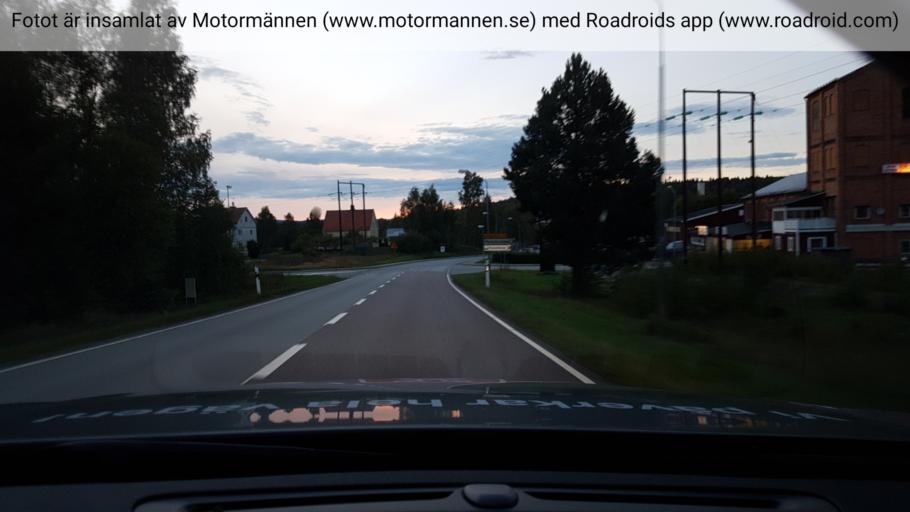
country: SE
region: OErebro
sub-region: Ljusnarsbergs Kommun
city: Kopparberg
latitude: 59.8704
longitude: 14.9926
